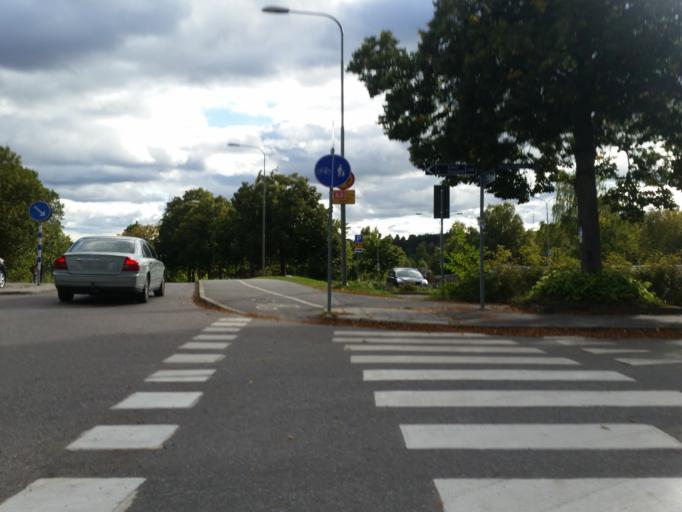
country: SE
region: Stockholm
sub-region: Stockholms Kommun
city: Arsta
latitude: 59.2729
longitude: 18.1097
